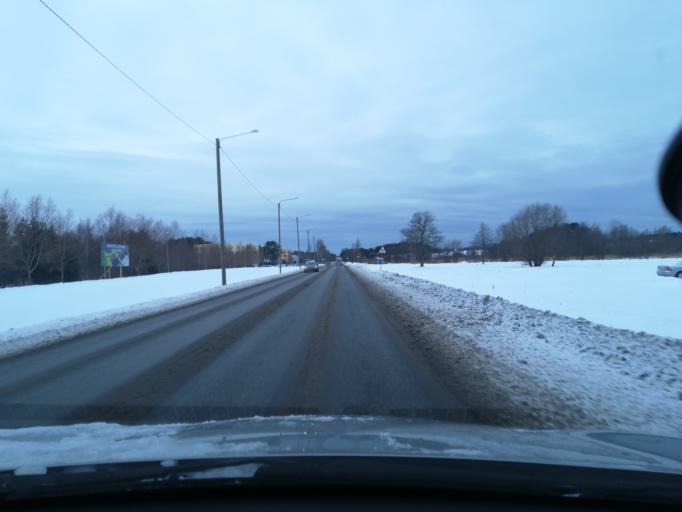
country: EE
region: Harju
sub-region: Saue vald
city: Laagri
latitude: 59.4294
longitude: 24.6162
